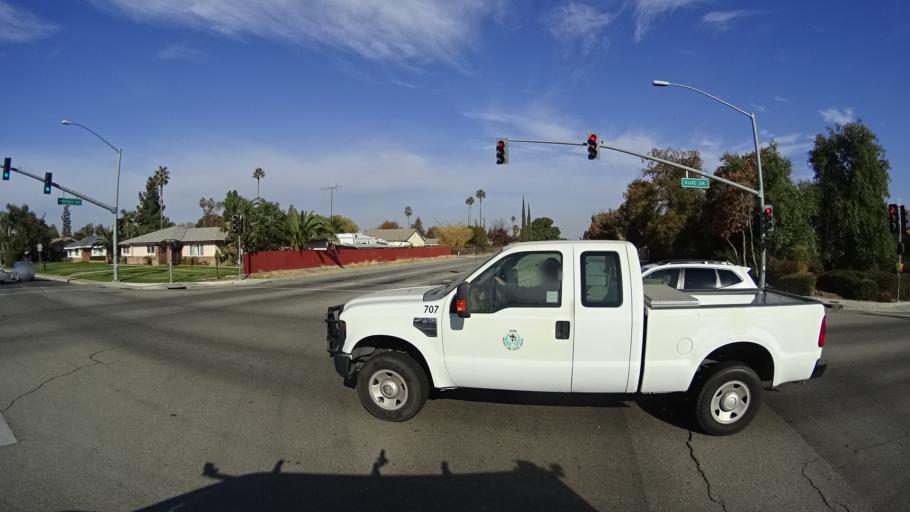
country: US
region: California
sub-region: Kern County
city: Greenacres
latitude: 35.4123
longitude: -119.0744
